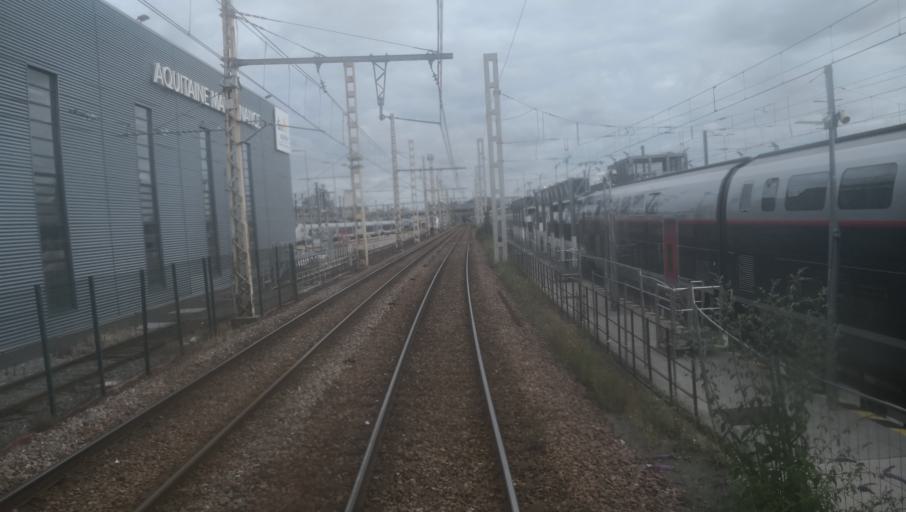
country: FR
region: Aquitaine
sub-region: Departement de la Gironde
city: Begles
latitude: 44.8176
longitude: -0.5593
